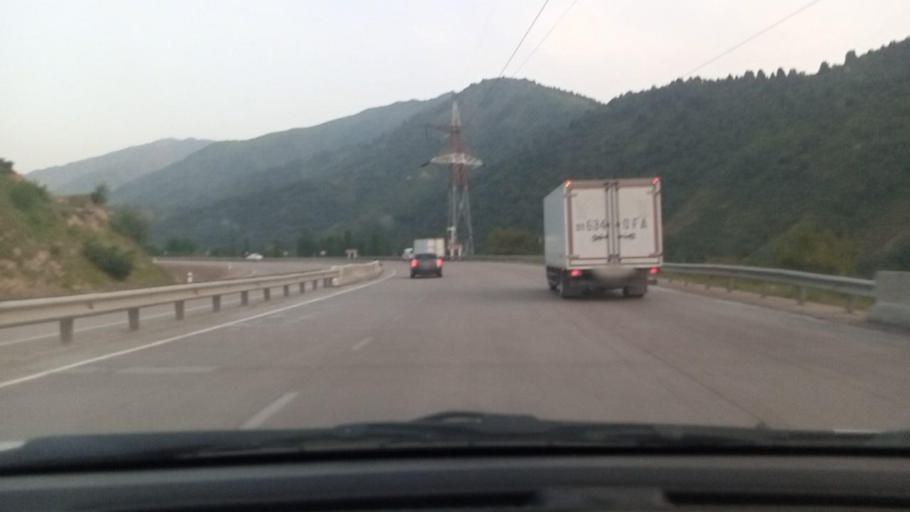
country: UZ
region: Toshkent
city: Angren
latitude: 41.1467
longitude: 70.4461
